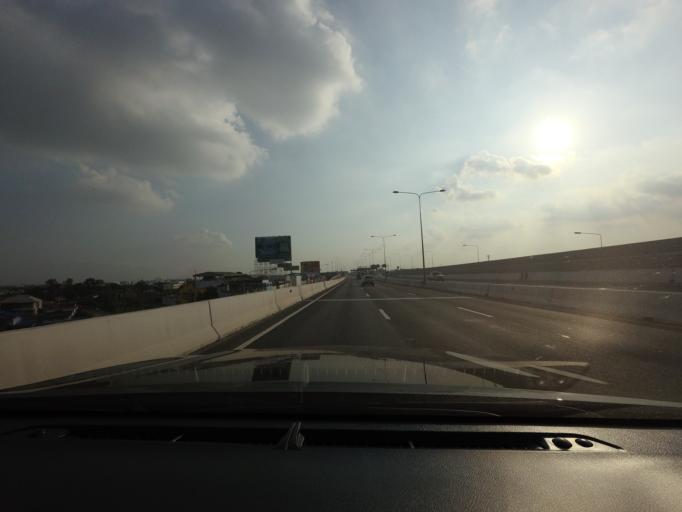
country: TH
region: Bangkok
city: Don Mueang
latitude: 13.9430
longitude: 100.6145
